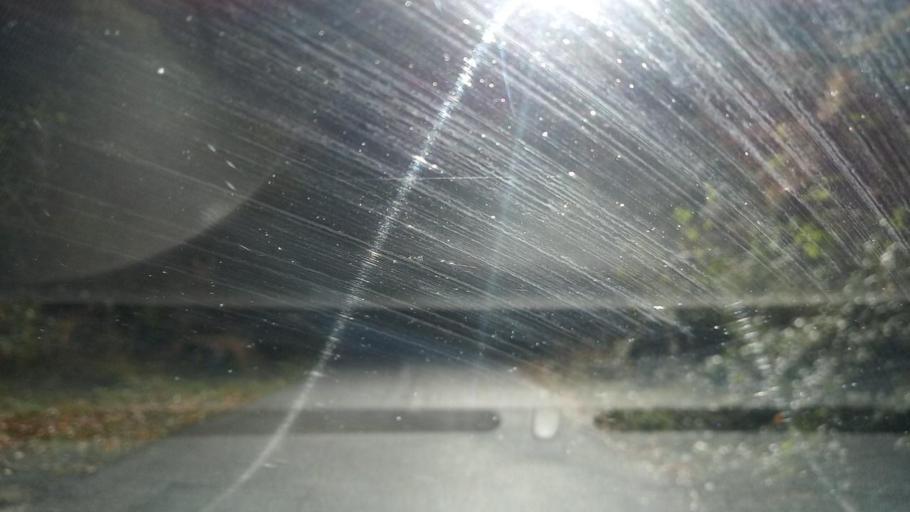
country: RO
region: Sibiu
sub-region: Comuna Boita
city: Boita
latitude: 45.5591
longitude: 24.2604
